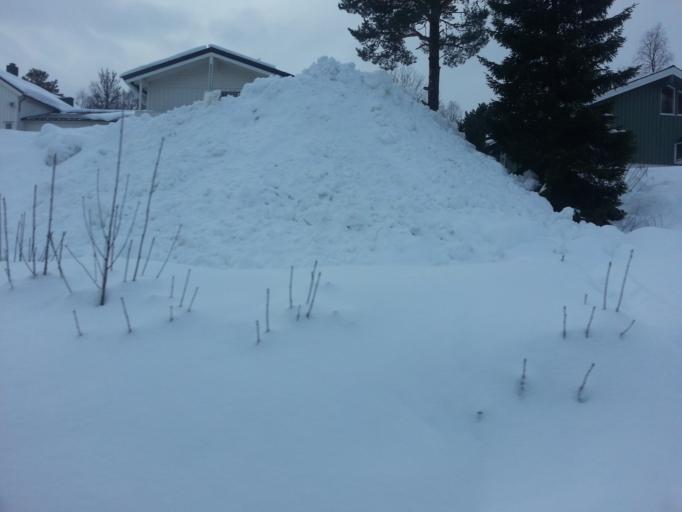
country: NO
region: Sor-Trondelag
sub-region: Trondheim
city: Trondheim
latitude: 63.4068
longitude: 10.3308
